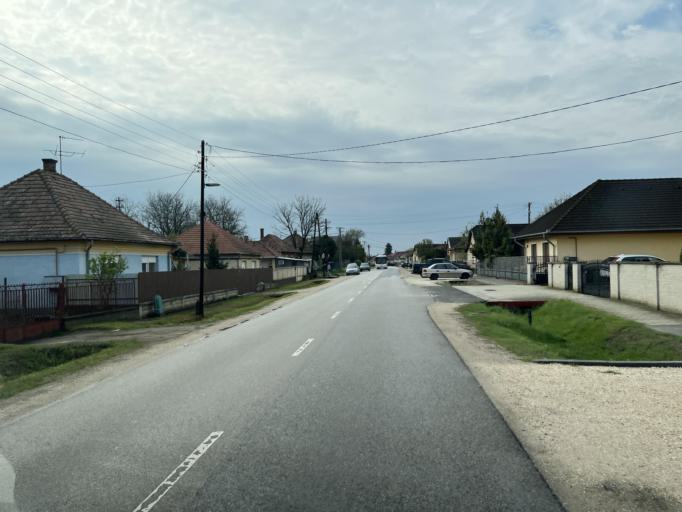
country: HU
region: Pest
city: Nyaregyhaza
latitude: 47.2326
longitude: 19.4480
